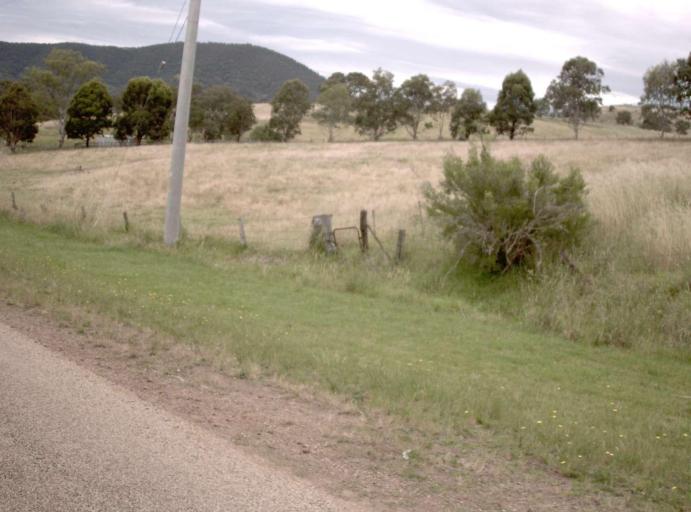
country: AU
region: Victoria
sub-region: East Gippsland
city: Bairnsdale
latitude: -37.4716
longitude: 147.2488
